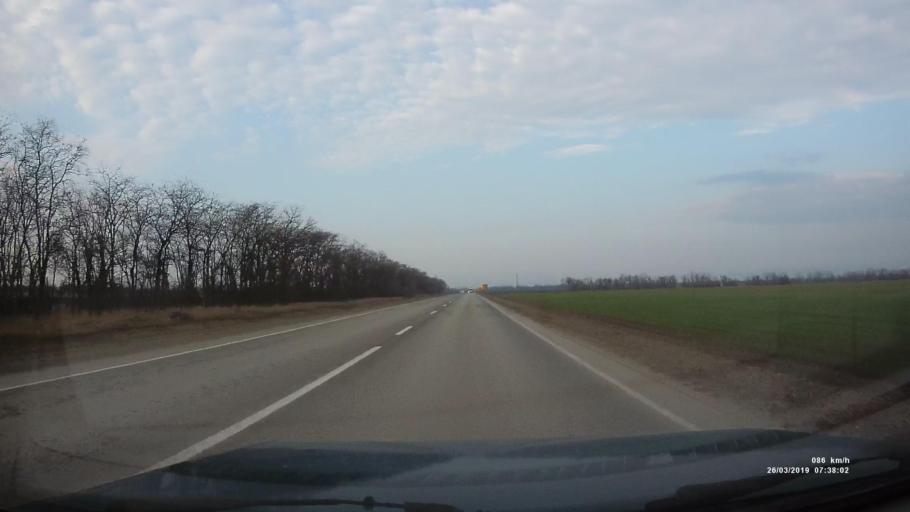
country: RU
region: Rostov
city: Novobessergenovka
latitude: 47.2013
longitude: 38.6896
